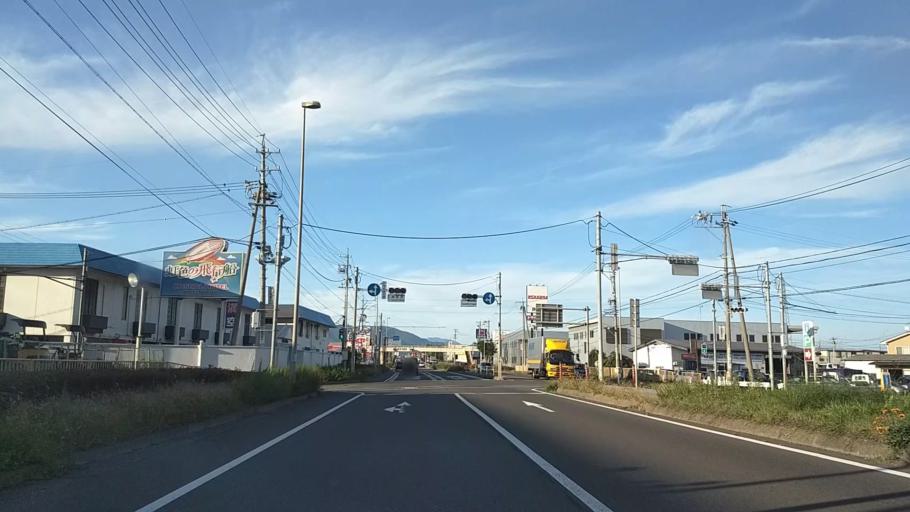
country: JP
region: Nagano
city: Nagano-shi
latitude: 36.6120
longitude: 138.1967
